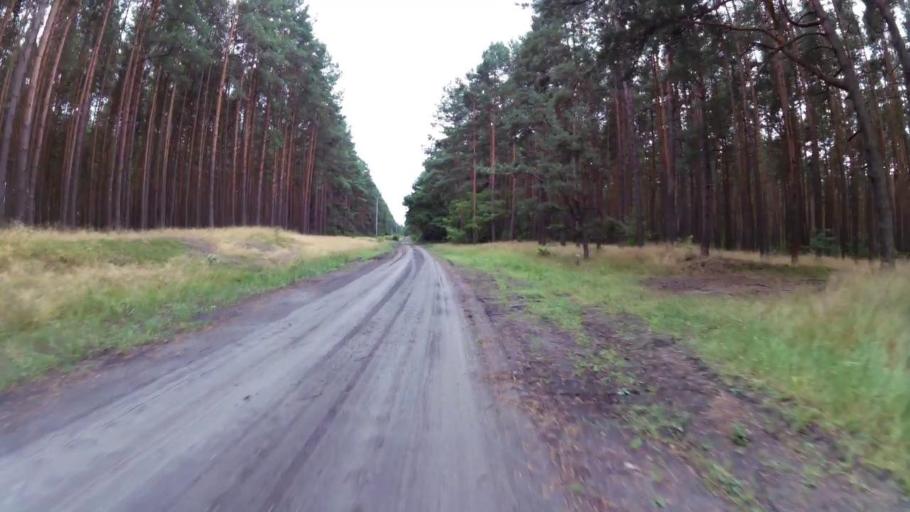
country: PL
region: West Pomeranian Voivodeship
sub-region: Powiat mysliborski
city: Debno
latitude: 52.8077
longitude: 14.7210
